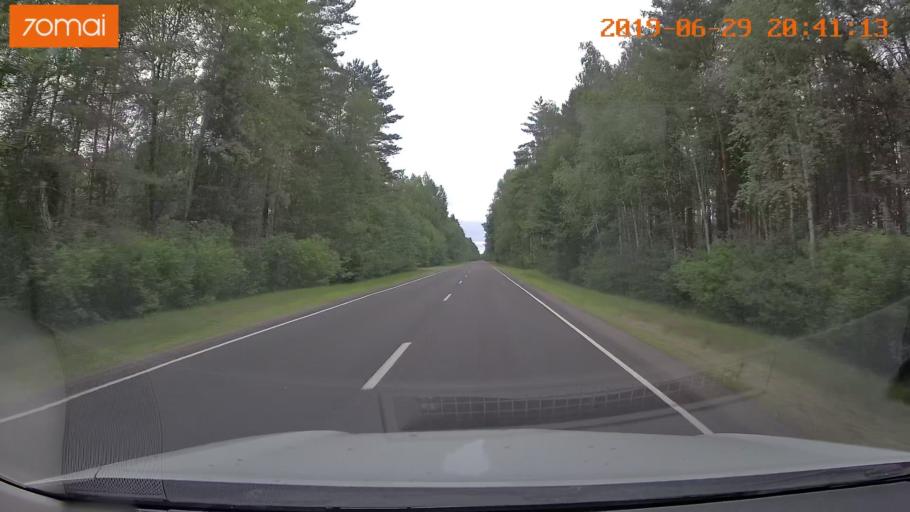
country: BY
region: Brest
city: Hantsavichy
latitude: 52.5831
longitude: 26.3422
